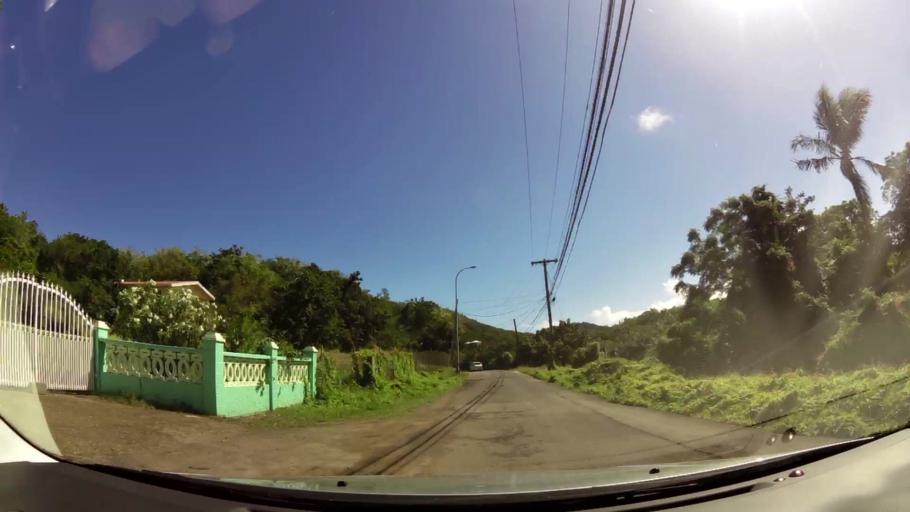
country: AG
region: Saint Paul
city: Falmouth
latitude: 17.0153
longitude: -61.7645
